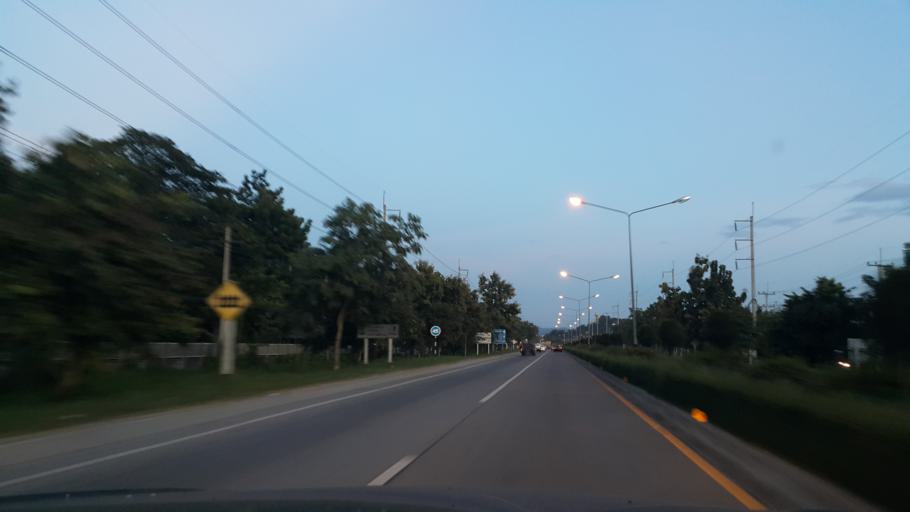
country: TH
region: Lamphun
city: Lamphun
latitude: 18.5556
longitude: 99.0430
